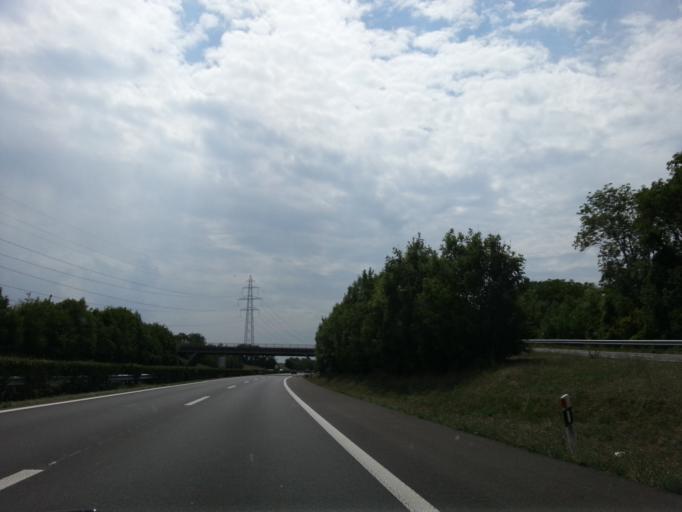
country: CH
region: Vaud
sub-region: Jura-Nord vaudois District
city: Chavornay
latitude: 46.7079
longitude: 6.5792
